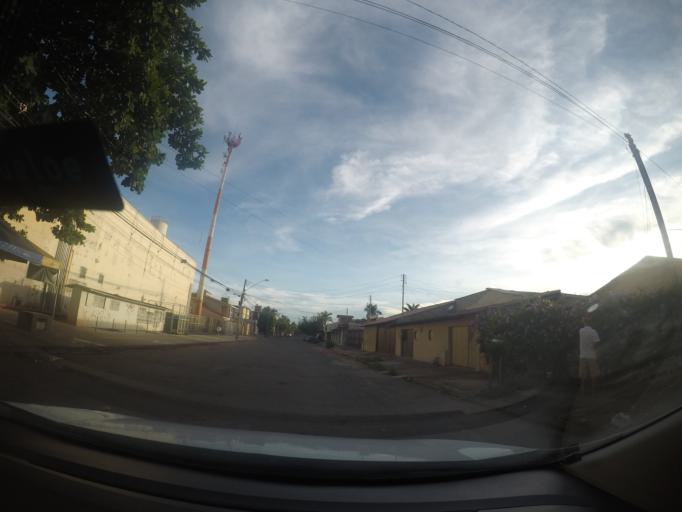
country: BR
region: Goias
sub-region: Goiania
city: Goiania
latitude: -16.6821
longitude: -49.3147
